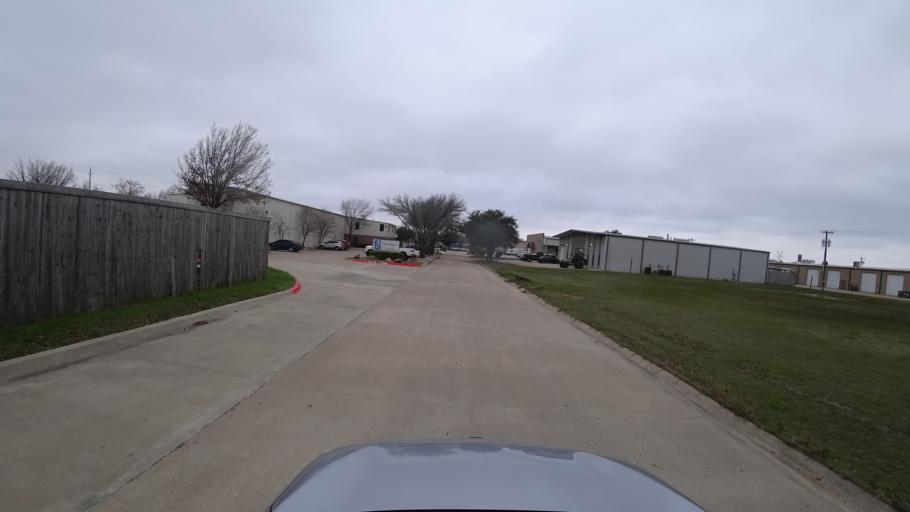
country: US
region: Texas
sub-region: Denton County
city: Lewisville
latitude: 33.0597
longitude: -96.9927
